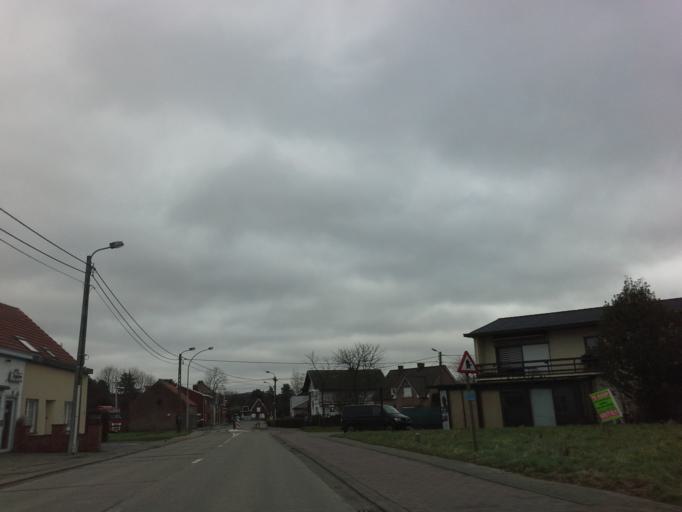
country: BE
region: Flanders
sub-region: Provincie Antwerpen
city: Heist-op-den-Berg
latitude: 51.0700
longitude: 4.7193
